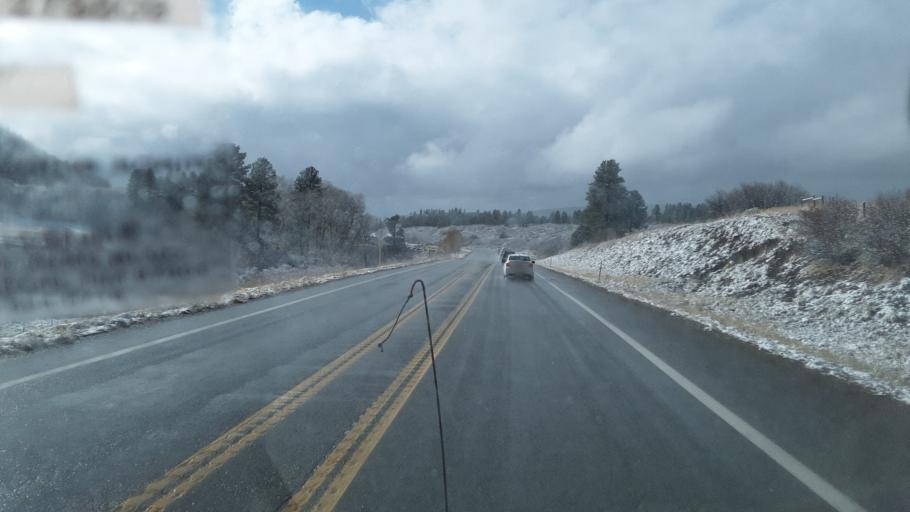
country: US
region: Colorado
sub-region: Archuleta County
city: Pagosa Springs
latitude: 37.2408
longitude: -107.1424
